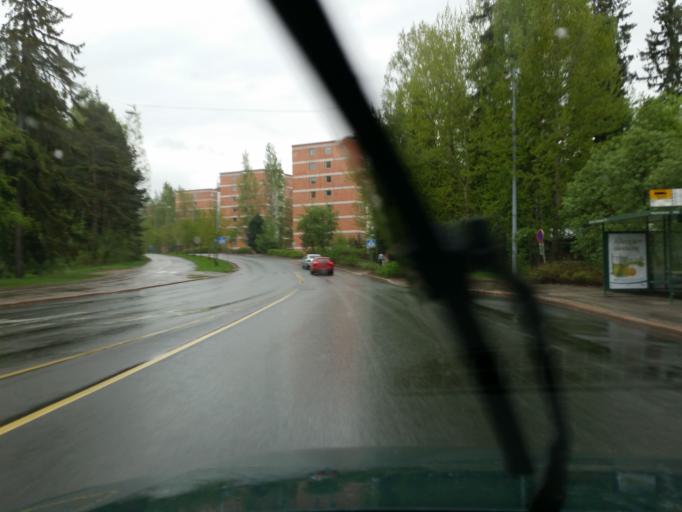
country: FI
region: Uusimaa
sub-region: Helsinki
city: Teekkarikylae
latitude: 60.2327
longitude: 24.8893
